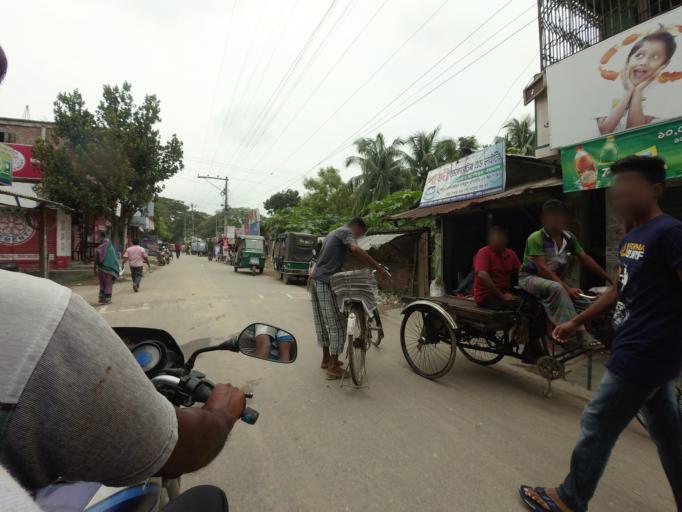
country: BD
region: Khulna
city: Kalia
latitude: 23.1803
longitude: 89.6478
